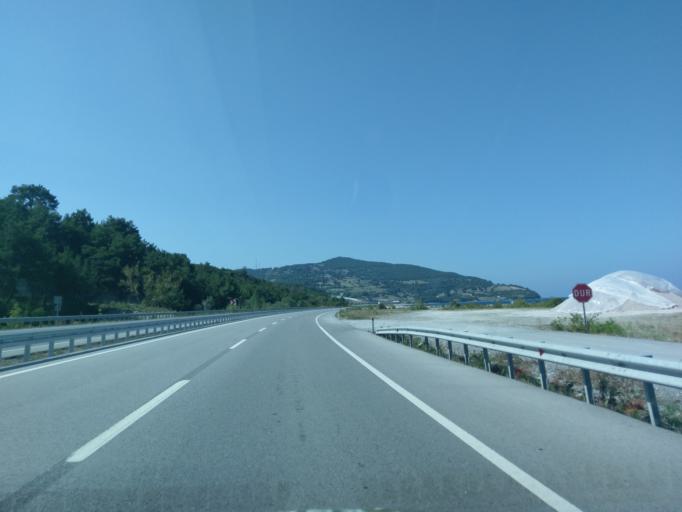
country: TR
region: Sinop
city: Dikmen
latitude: 41.7163
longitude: 35.2756
